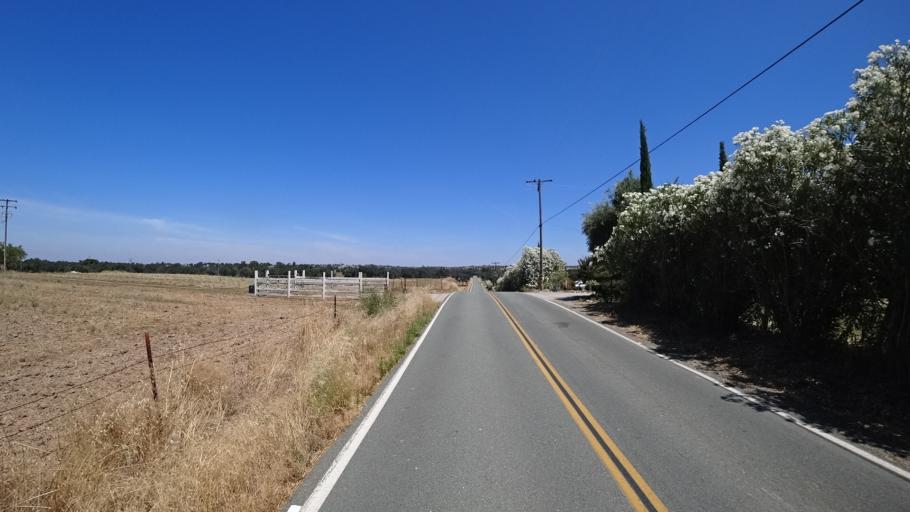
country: US
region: California
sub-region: Calaveras County
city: Rancho Calaveras
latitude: 38.1653
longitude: -120.9182
